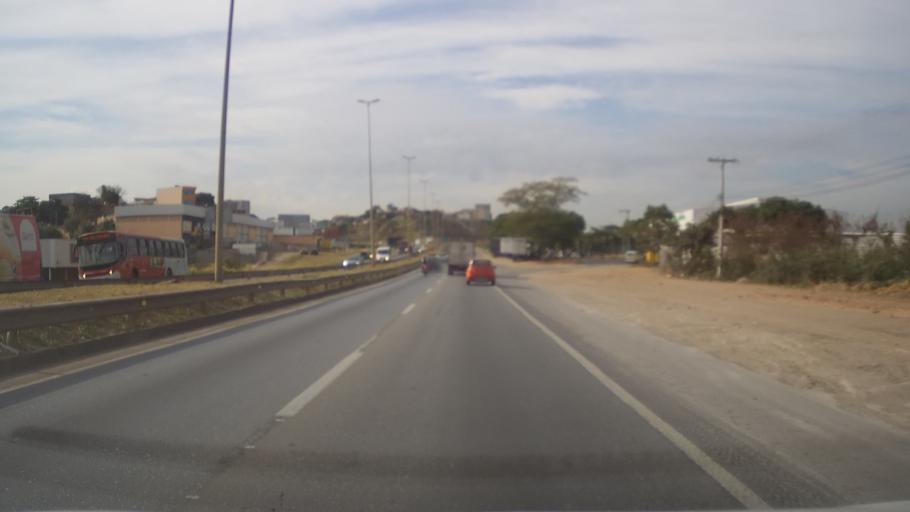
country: BR
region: Minas Gerais
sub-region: Contagem
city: Contagem
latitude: -19.9159
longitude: -44.0399
